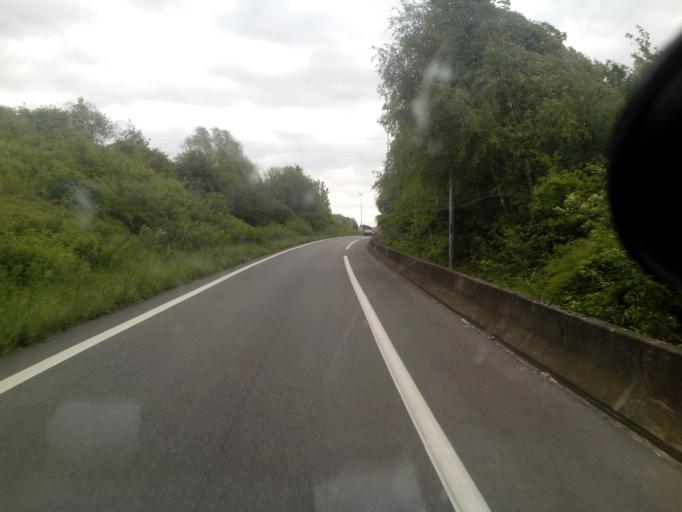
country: FR
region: Nord-Pas-de-Calais
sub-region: Departement du Nord
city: Wasquehal
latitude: 50.6578
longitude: 3.1157
